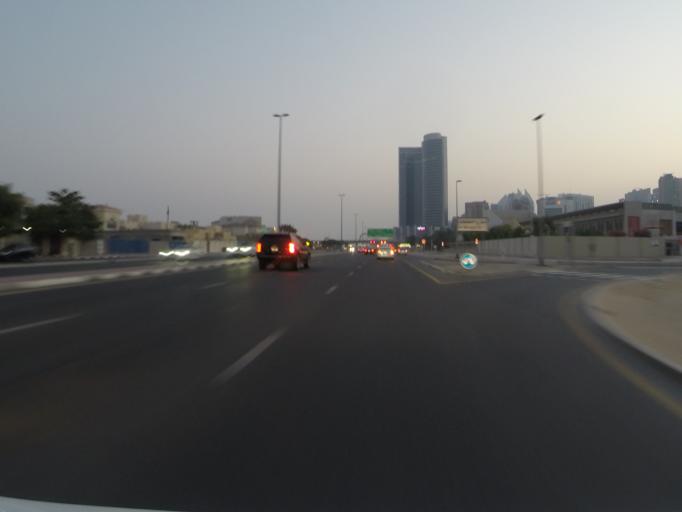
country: AE
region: Dubai
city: Dubai
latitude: 25.1011
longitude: 55.1852
